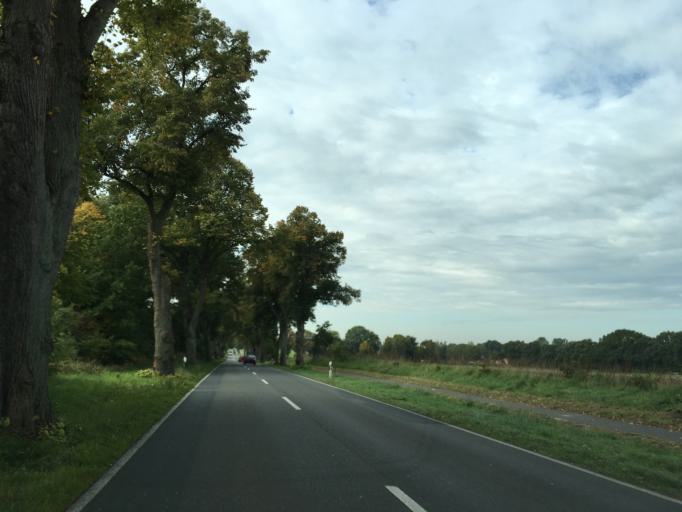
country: DE
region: Lower Saxony
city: Adendorf
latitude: 53.2700
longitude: 10.4711
